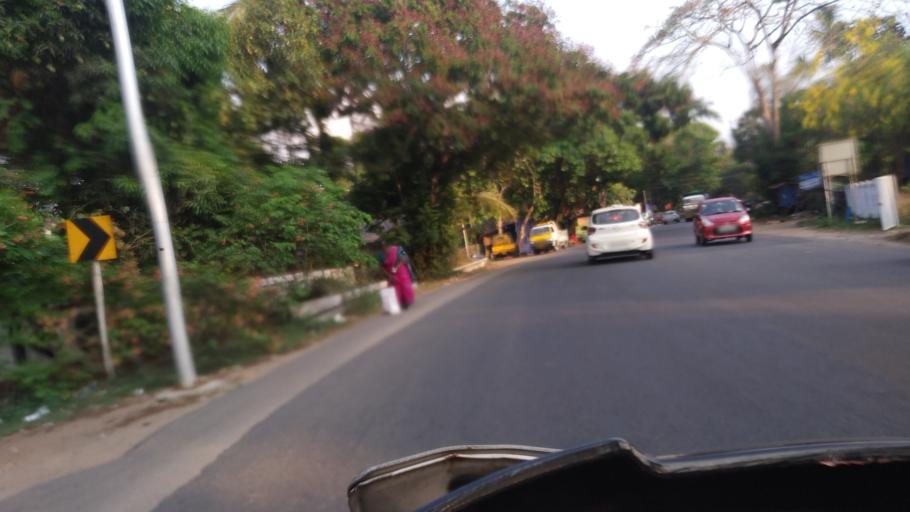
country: IN
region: Kerala
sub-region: Thrissur District
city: Irinjalakuda
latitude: 10.3131
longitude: 76.1489
